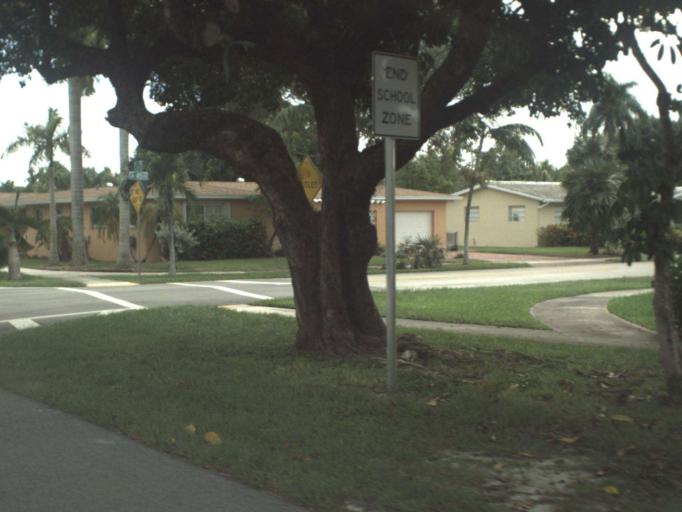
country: US
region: Florida
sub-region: Miami-Dade County
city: Coral Gables
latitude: 25.7290
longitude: -80.2863
